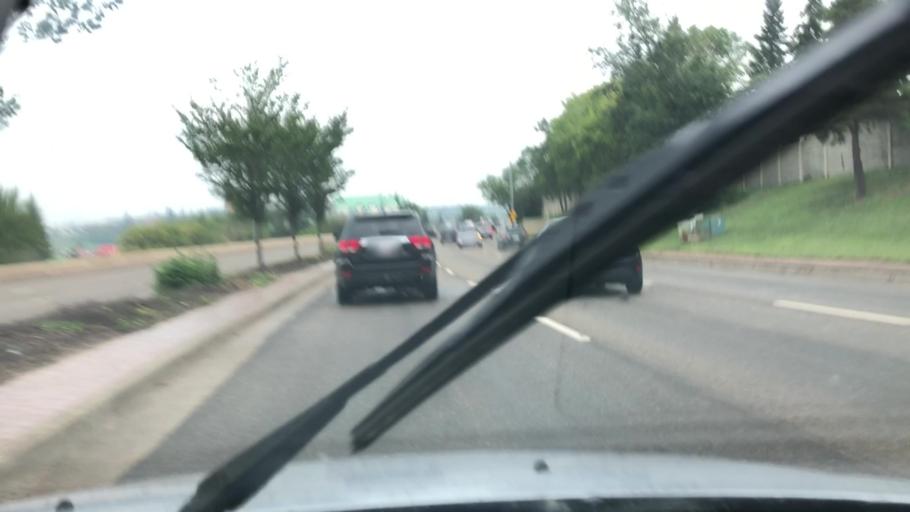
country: CA
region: Alberta
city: St. Albert
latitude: 53.6306
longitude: -113.6216
